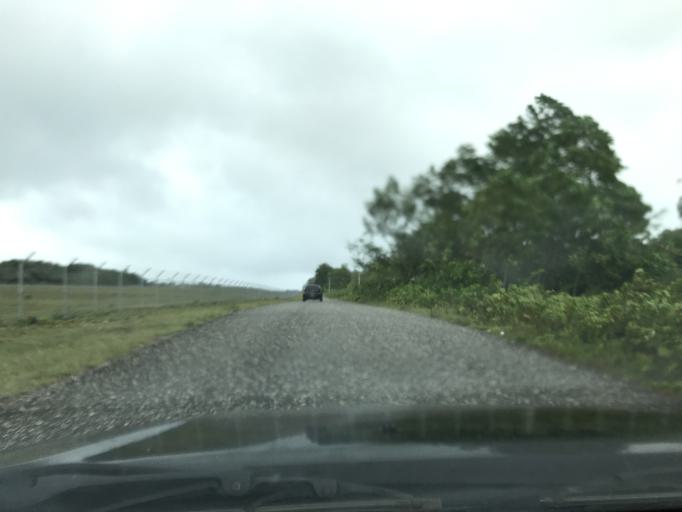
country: SB
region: Western Province
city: Gizo
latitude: -8.3259
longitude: 157.2640
